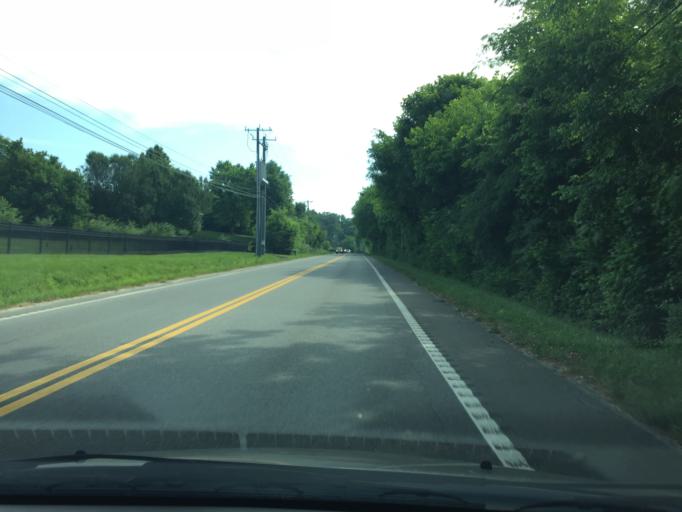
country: US
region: Tennessee
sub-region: Hamilton County
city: Collegedale
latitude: 35.0809
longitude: -85.0313
